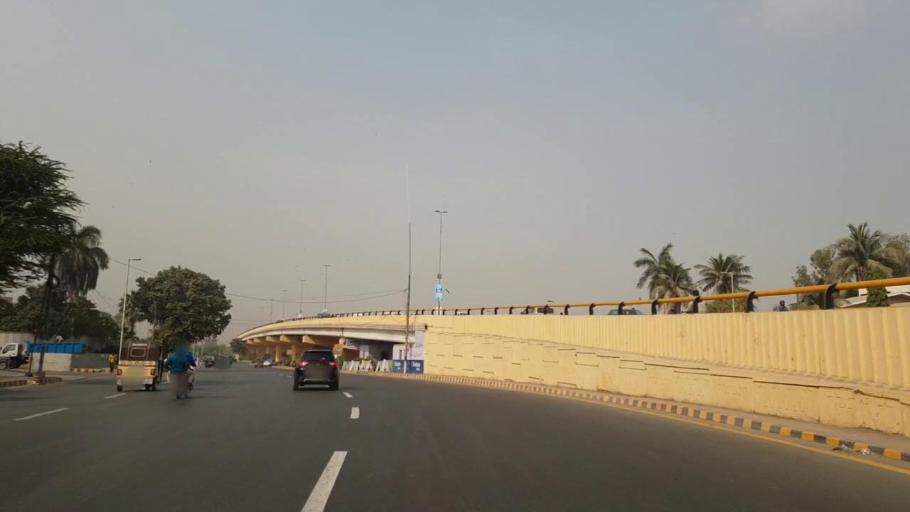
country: PK
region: Sindh
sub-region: Karachi District
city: Karachi
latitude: 24.8917
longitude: 67.0844
